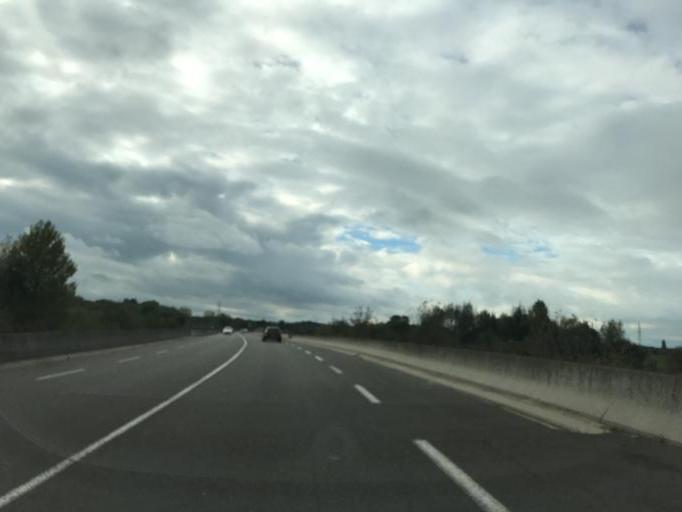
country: FR
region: Rhone-Alpes
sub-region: Departement de l'Ain
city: Viriat
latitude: 46.2306
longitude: 5.2219
